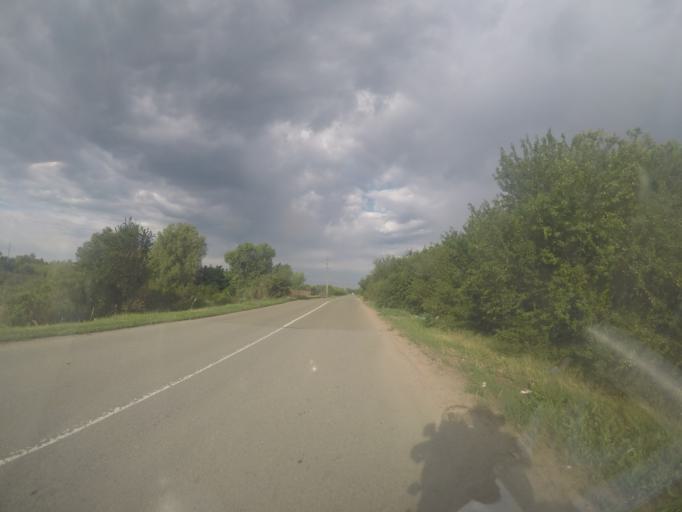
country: RS
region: Central Serbia
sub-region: Belgrade
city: Zemun
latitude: 44.9148
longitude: 20.4374
